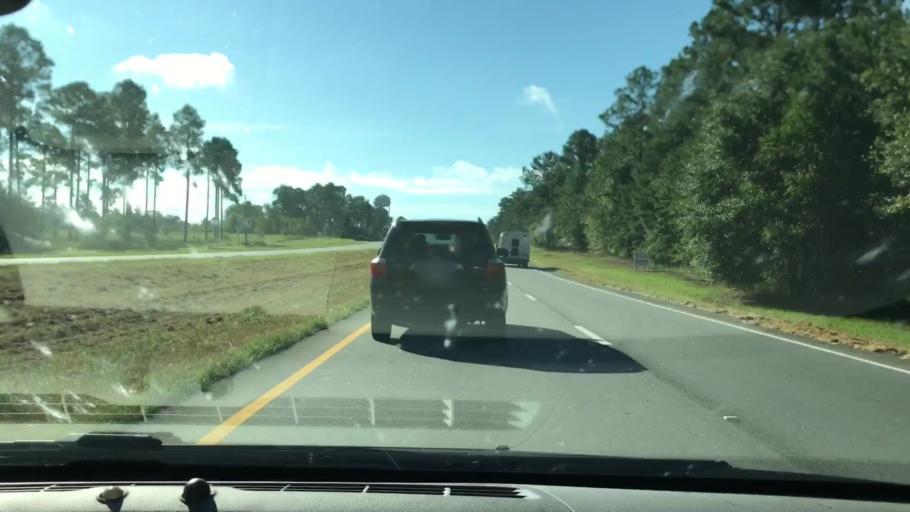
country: US
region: Georgia
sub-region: Dougherty County
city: Albany
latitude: 31.6445
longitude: -84.2569
